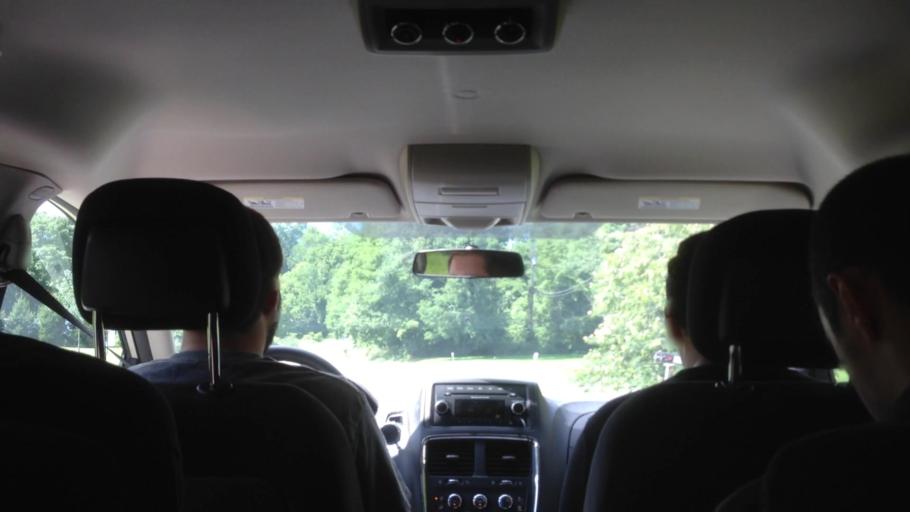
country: US
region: New York
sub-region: Dutchess County
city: Tivoli
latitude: 42.0559
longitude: -73.8933
